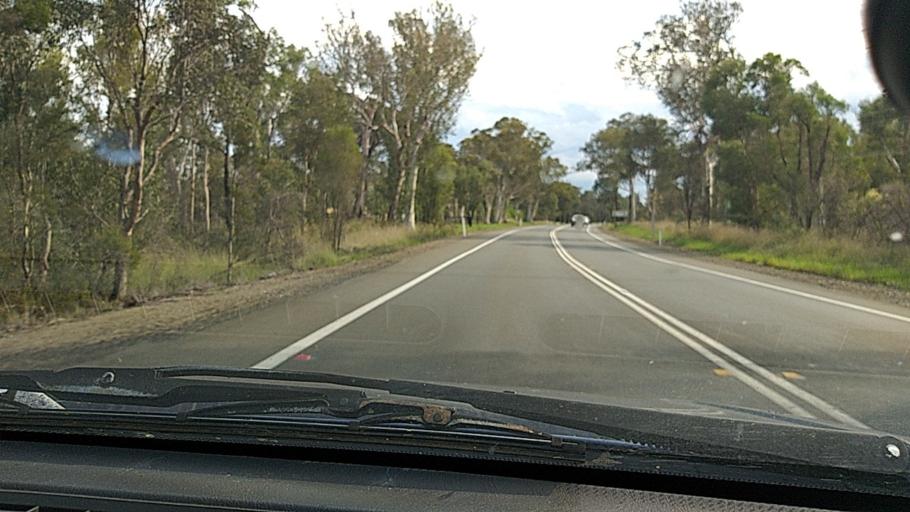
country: AU
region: New South Wales
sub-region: Penrith Municipality
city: Werrington Downs
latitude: -33.6826
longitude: 150.7397
